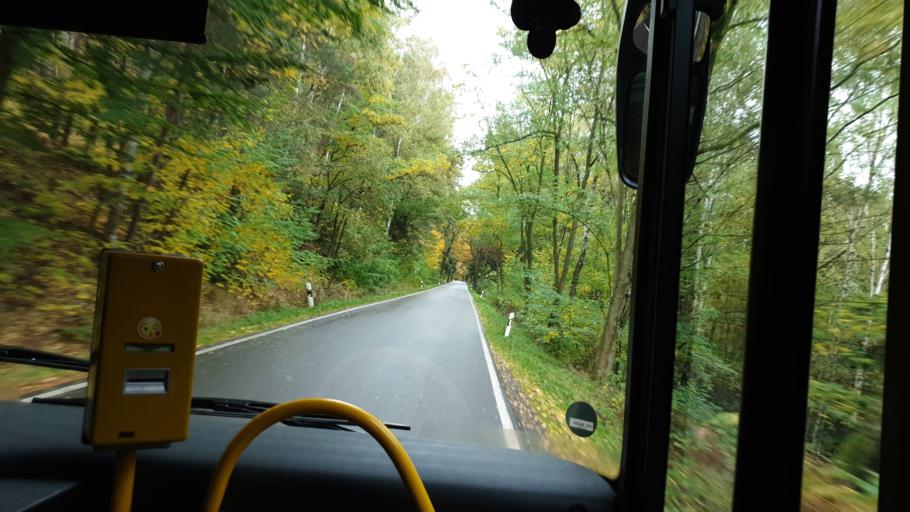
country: DE
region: Saxony
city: Kurort Gohrisch
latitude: 50.8896
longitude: 14.1034
